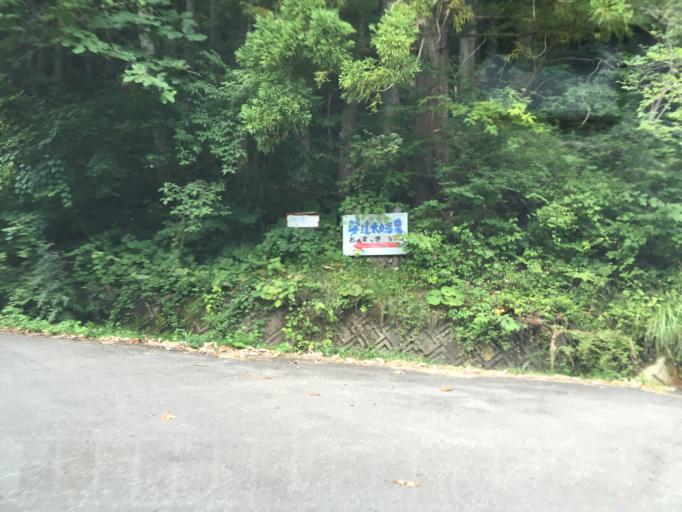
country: JP
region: Fukushima
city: Motomiya
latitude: 37.5873
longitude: 140.3345
